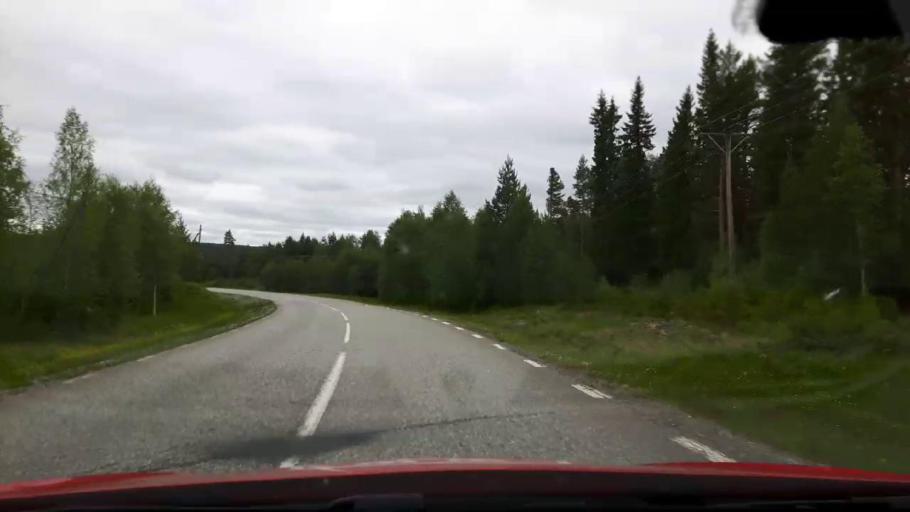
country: SE
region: Jaemtland
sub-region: Stroemsunds Kommun
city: Stroemsund
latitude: 63.3051
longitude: 15.7584
